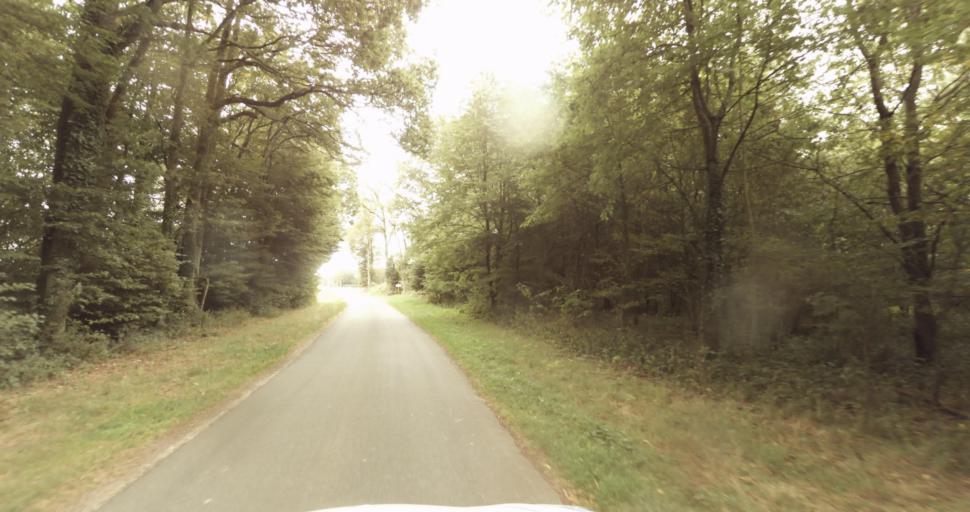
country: FR
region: Haute-Normandie
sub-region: Departement de l'Eure
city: La Madeleine-de-Nonancourt
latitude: 48.8159
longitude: 1.2078
